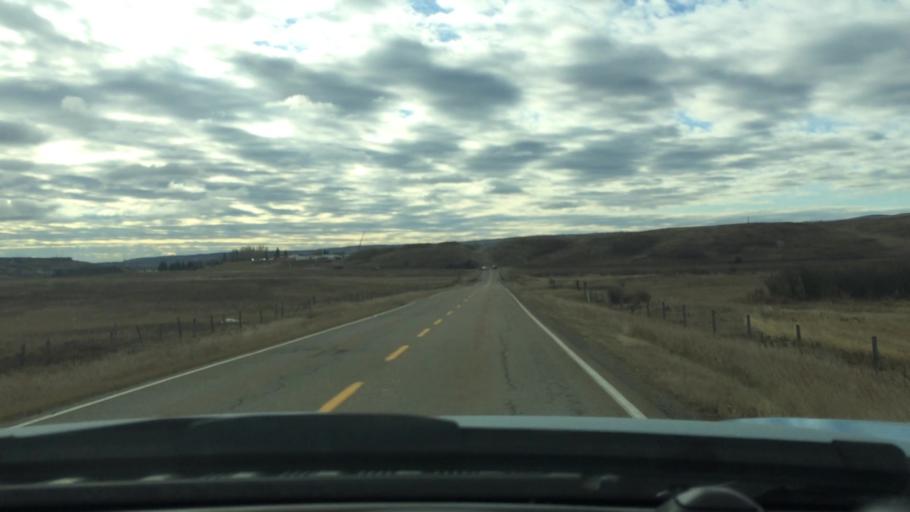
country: CA
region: Alberta
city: Airdrie
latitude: 51.1927
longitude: -114.1412
